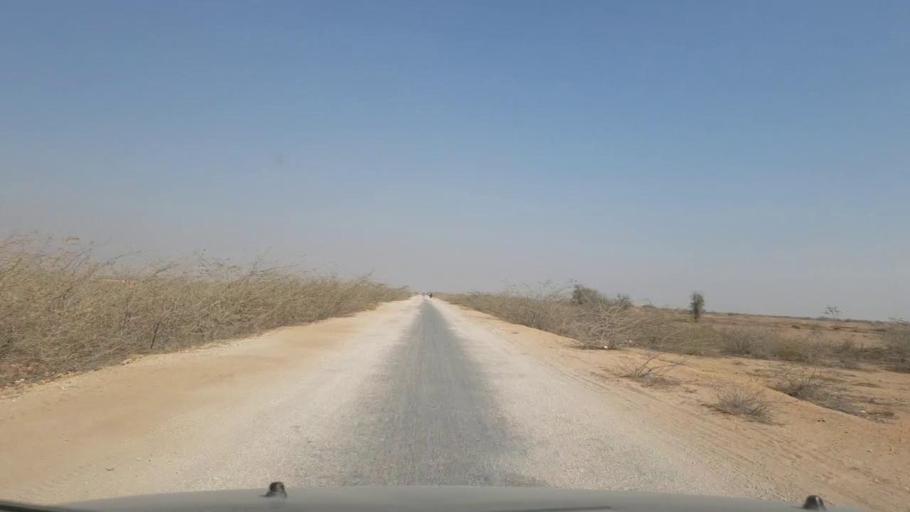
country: PK
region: Sindh
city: Thatta
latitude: 24.9050
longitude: 67.9249
